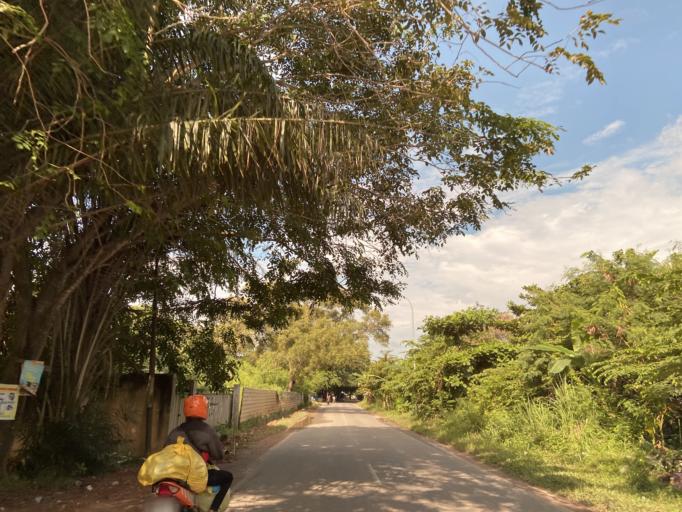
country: SG
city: Singapore
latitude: 1.1121
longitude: 104.0371
